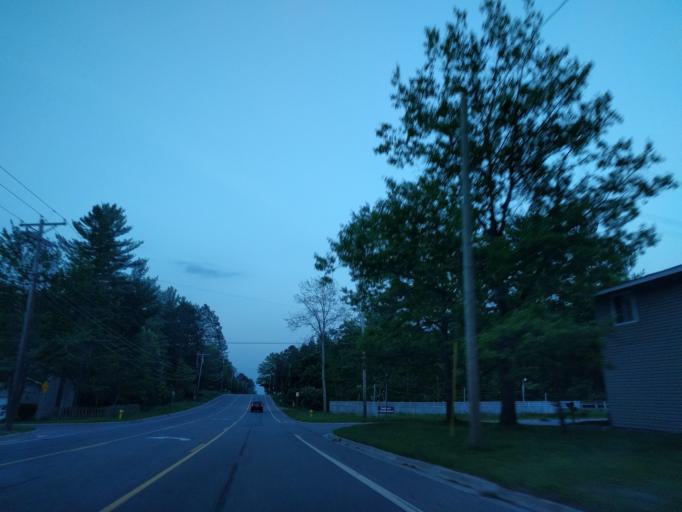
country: US
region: Michigan
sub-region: Marquette County
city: Trowbridge Park
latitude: 46.5641
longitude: -87.4300
